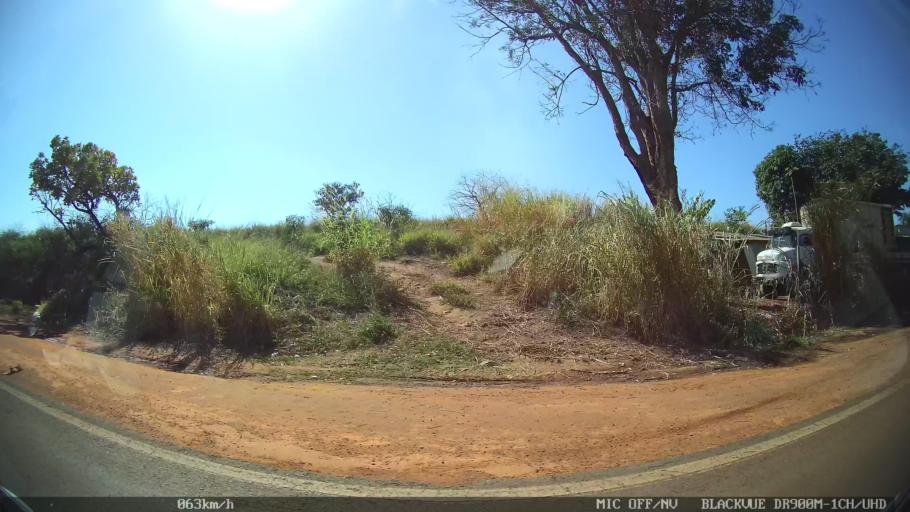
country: BR
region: Sao Paulo
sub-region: Batatais
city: Batatais
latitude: -20.8778
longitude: -47.6046
